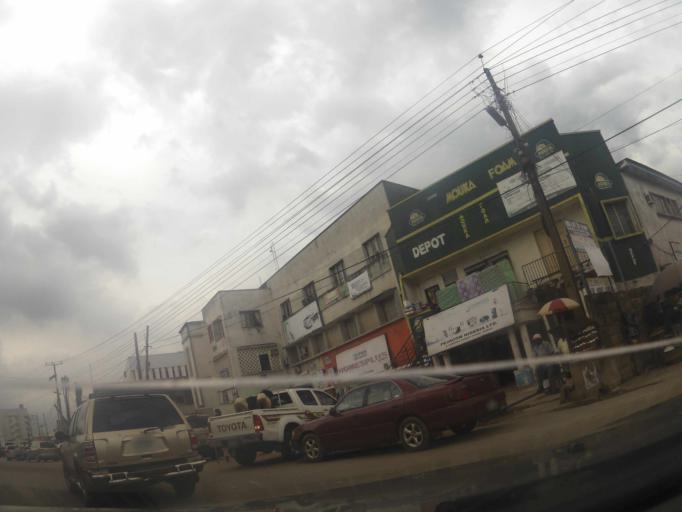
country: NG
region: Oyo
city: Ibadan
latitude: 7.3883
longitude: 3.8814
